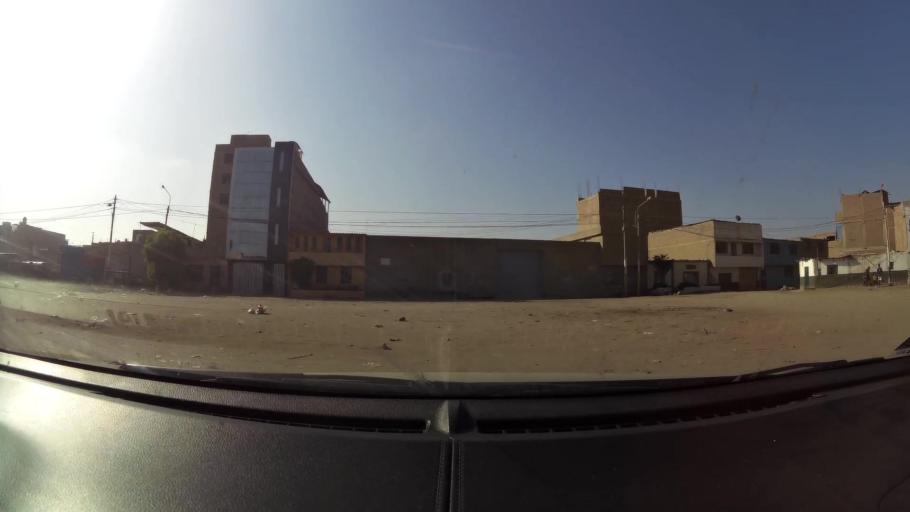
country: PE
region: Lambayeque
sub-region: Provincia de Chiclayo
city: Chiclayo
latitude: -6.7637
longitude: -79.8473
